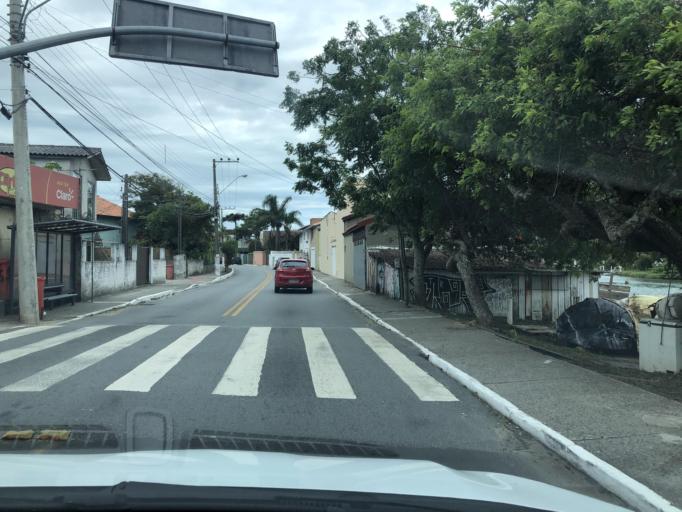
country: BR
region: Santa Catarina
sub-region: Florianopolis
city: Lagoa
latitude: -27.5841
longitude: -48.4359
